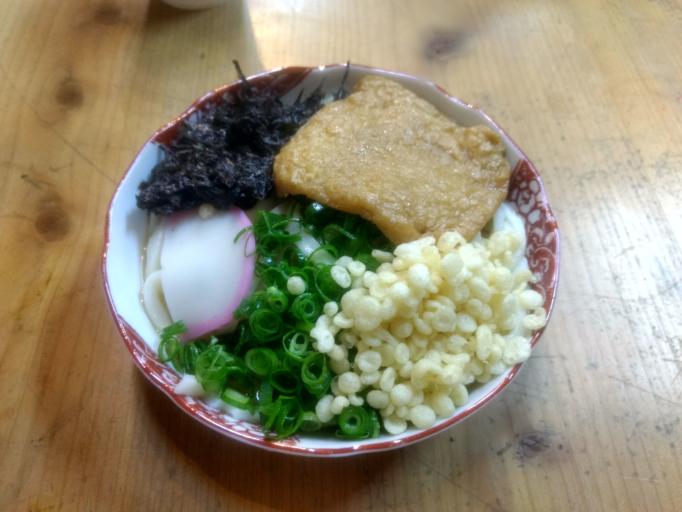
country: JP
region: Kyoto
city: Miyazu
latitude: 35.5484
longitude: 135.0783
